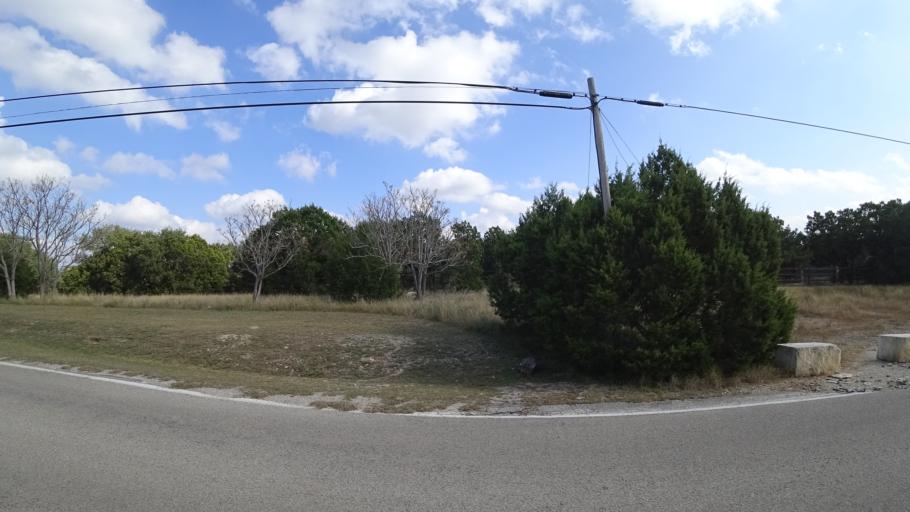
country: US
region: Texas
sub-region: Travis County
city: Barton Creek
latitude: 30.3039
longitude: -97.8636
